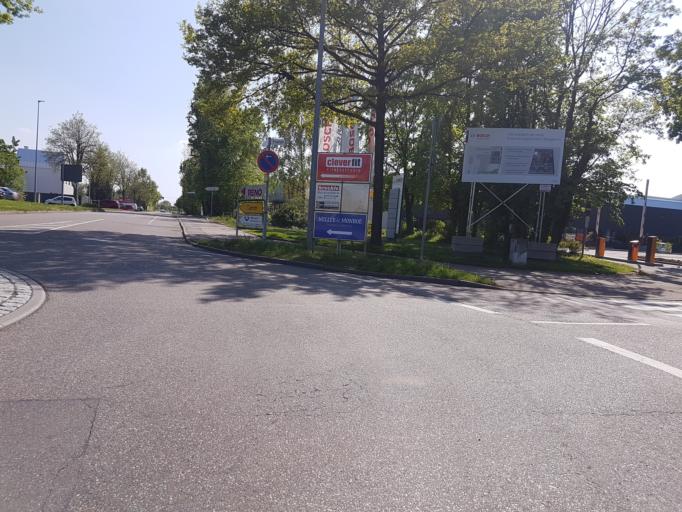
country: DE
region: Baden-Wuerttemberg
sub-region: Regierungsbezirk Stuttgart
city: Bietigheim-Bissingen
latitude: 48.9437
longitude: 9.1381
